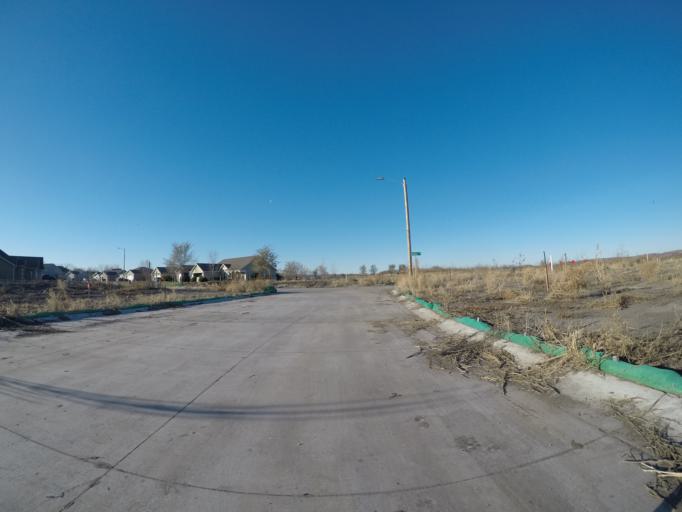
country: US
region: Kansas
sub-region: Riley County
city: Manhattan
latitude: 39.2195
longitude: -96.5712
